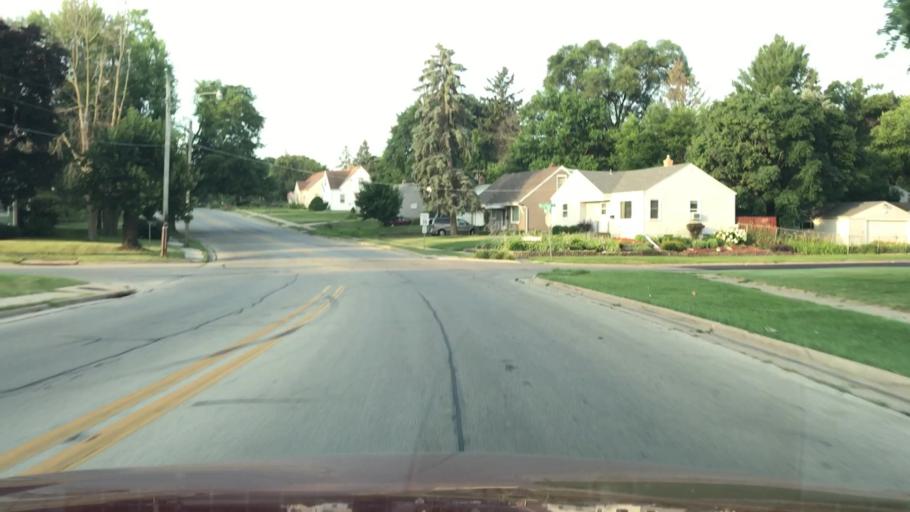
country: US
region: Illinois
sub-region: Winnebago County
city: Rockford
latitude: 42.2602
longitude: -89.0427
